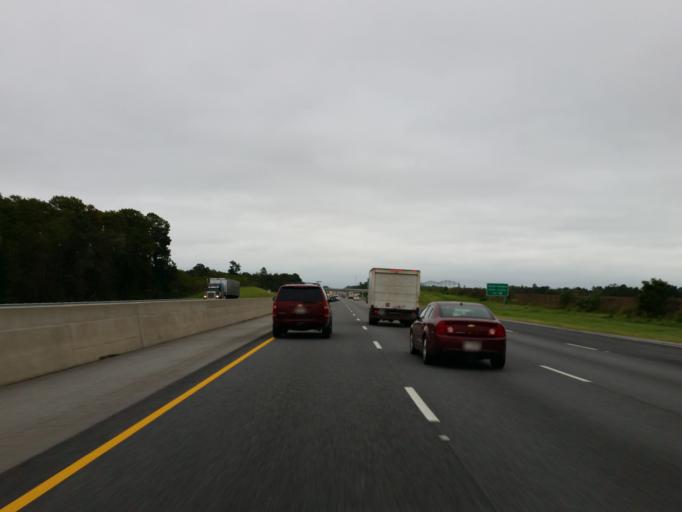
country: US
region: Georgia
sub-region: Turner County
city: Ashburn
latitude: 31.6802
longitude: -83.6195
